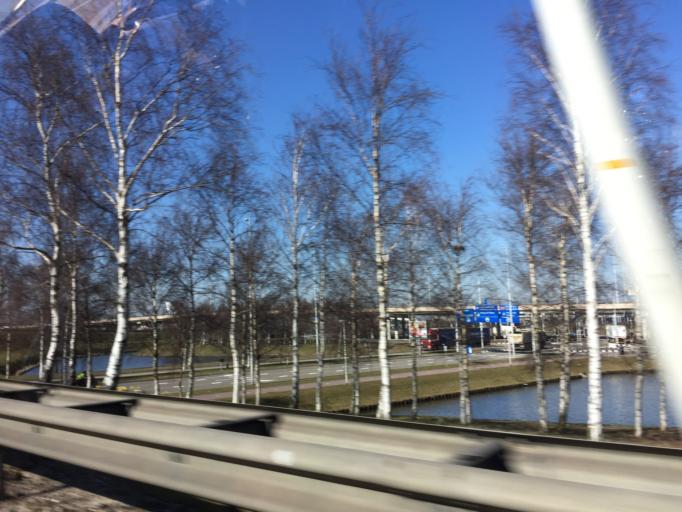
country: NL
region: North Holland
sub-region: Gemeente Aalsmeer
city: Aalsmeer
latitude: 52.3074
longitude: 4.7515
